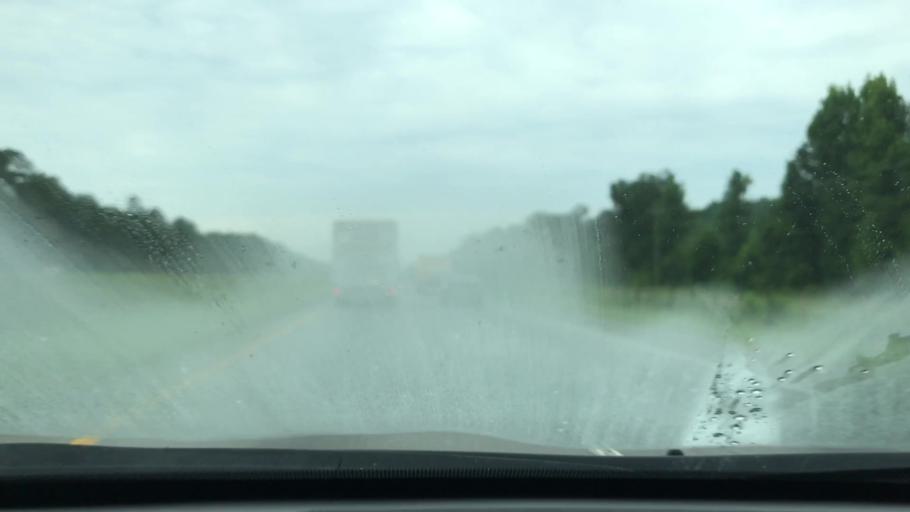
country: US
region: South Carolina
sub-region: Jasper County
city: Ridgeland
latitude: 32.5510
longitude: -80.9484
